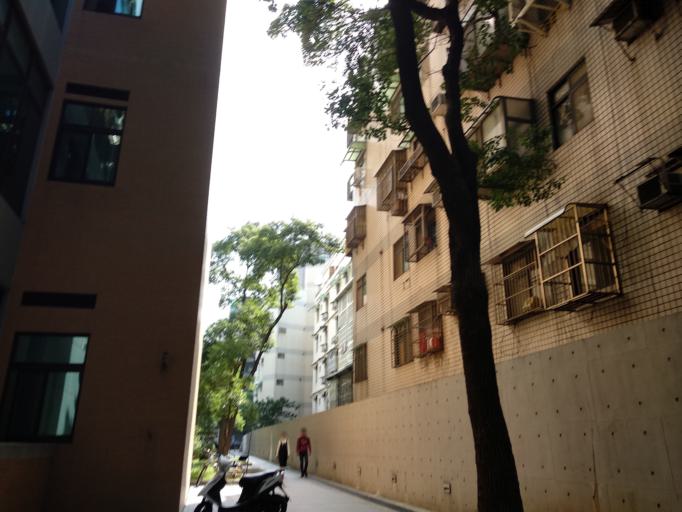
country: TW
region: Taiwan
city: Taoyuan City
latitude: 24.9570
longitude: 121.2408
